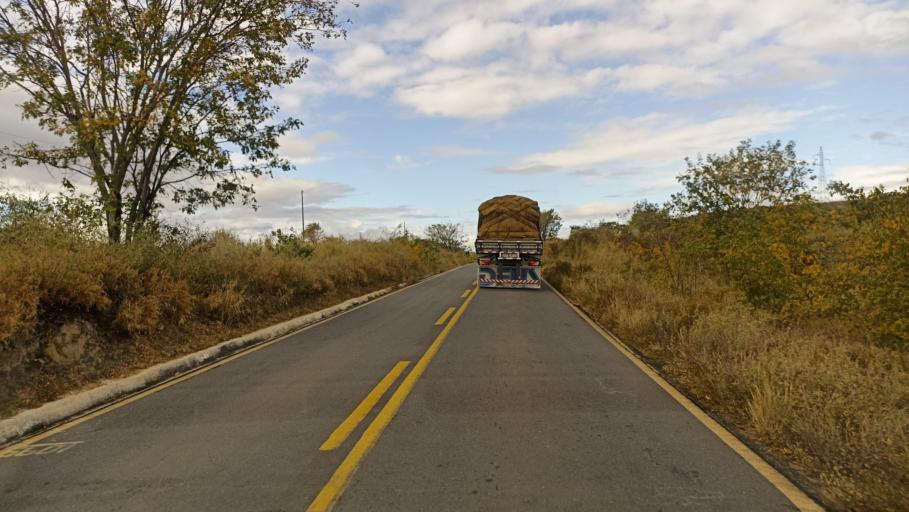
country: BR
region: Minas Gerais
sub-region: Itinga
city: Itinga
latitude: -16.5948
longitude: -41.6978
